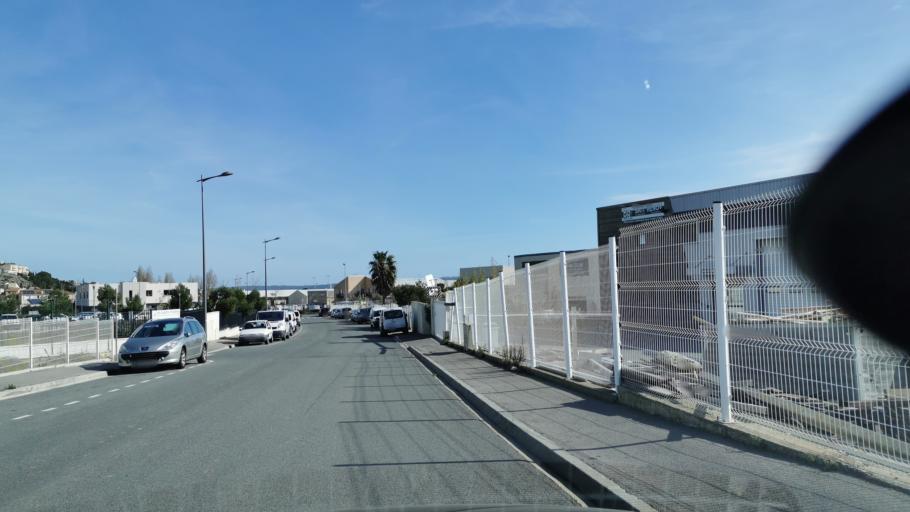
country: FR
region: Languedoc-Roussillon
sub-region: Departement de l'Aude
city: Narbonne
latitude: 43.1586
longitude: 2.9675
